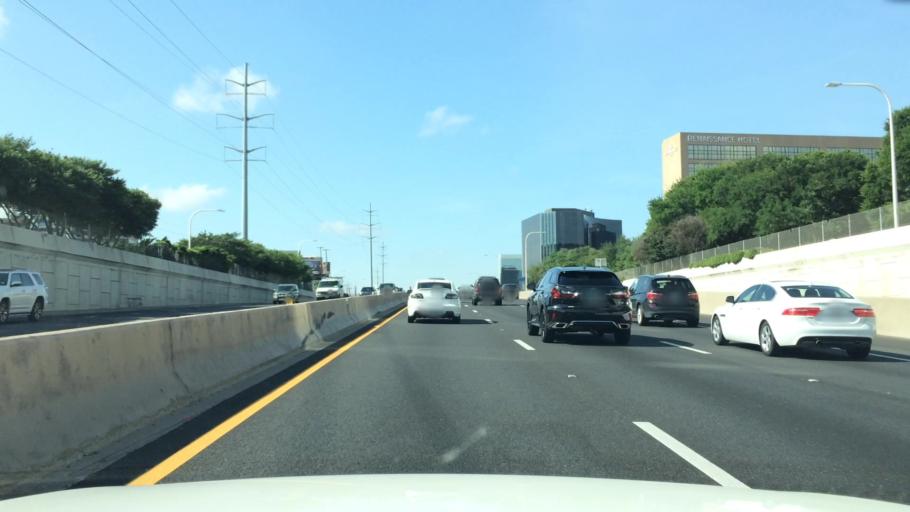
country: US
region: Texas
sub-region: Dallas County
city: Addison
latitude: 32.9587
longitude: -96.8212
